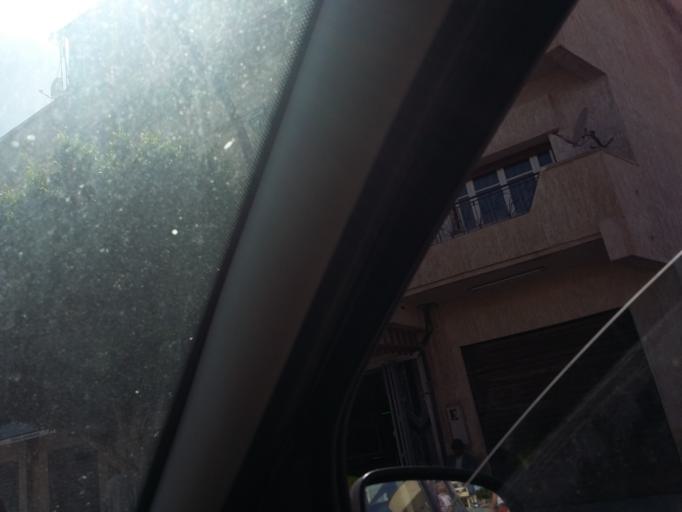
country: MA
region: Fes-Boulemane
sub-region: Fes
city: Fes
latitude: 34.0266
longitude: -5.0040
